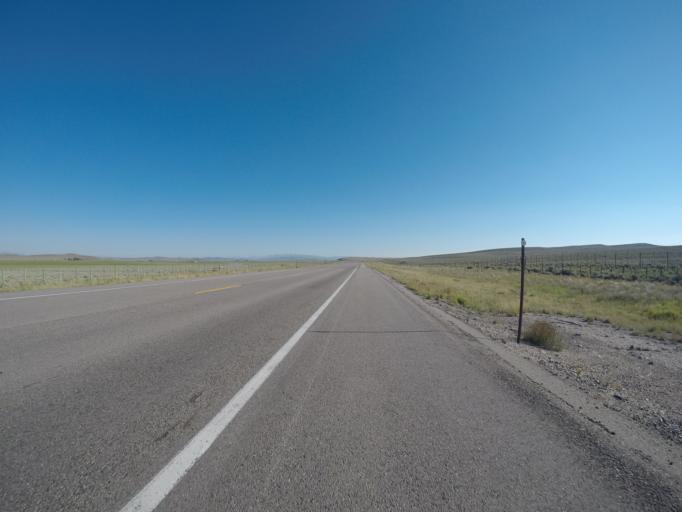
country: US
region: Wyoming
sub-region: Sublette County
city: Pinedale
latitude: 42.9268
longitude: -110.0809
